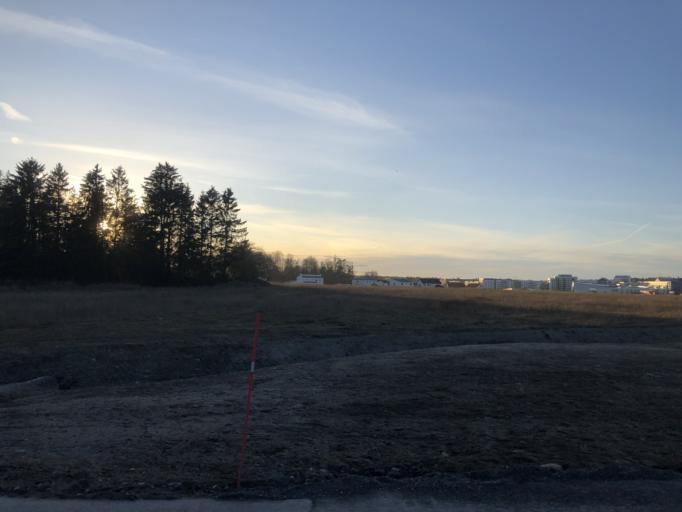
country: SE
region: Stockholm
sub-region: Jarfalla Kommun
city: Jakobsberg
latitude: 59.4125
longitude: 17.8840
